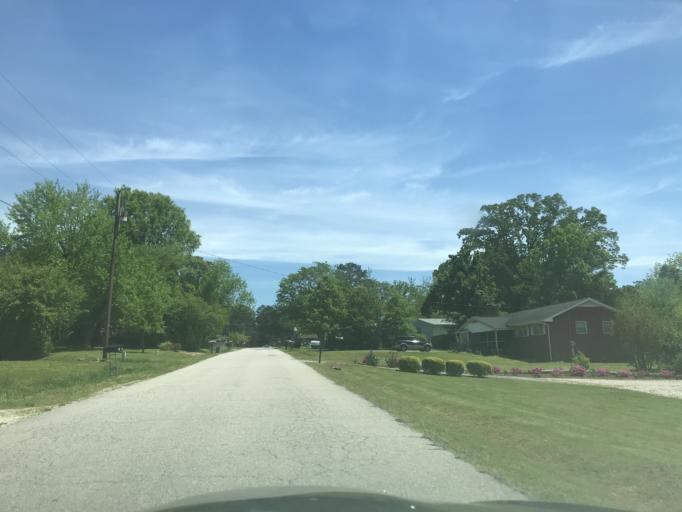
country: US
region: North Carolina
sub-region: Wake County
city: Raleigh
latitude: 35.8244
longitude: -78.5718
